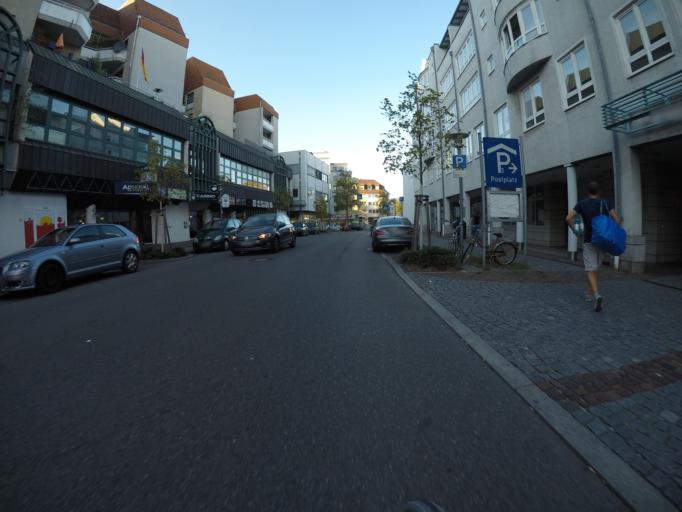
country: DE
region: Baden-Wuerttemberg
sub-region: Regierungsbezirk Stuttgart
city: Boeblingen
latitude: 48.6864
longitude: 9.0156
